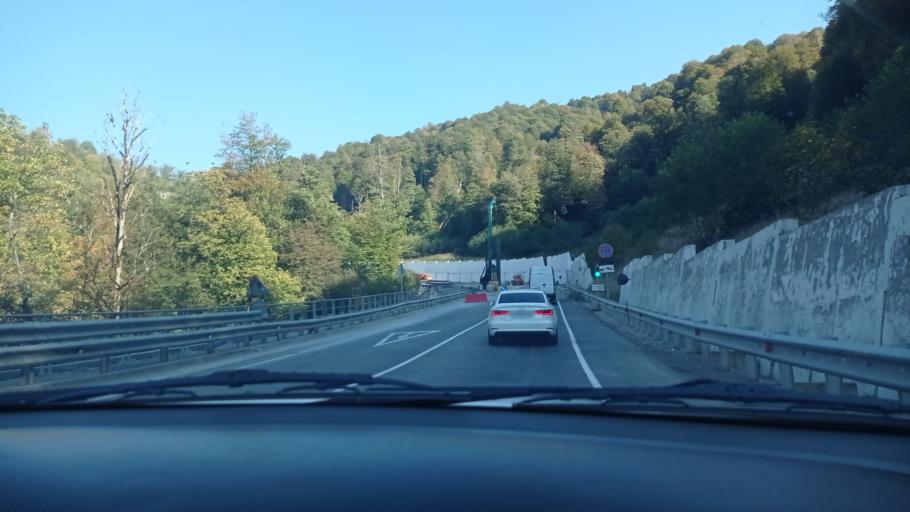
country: RU
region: Krasnodarskiy
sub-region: Sochi City
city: Krasnaya Polyana
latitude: 43.6598
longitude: 40.3059
